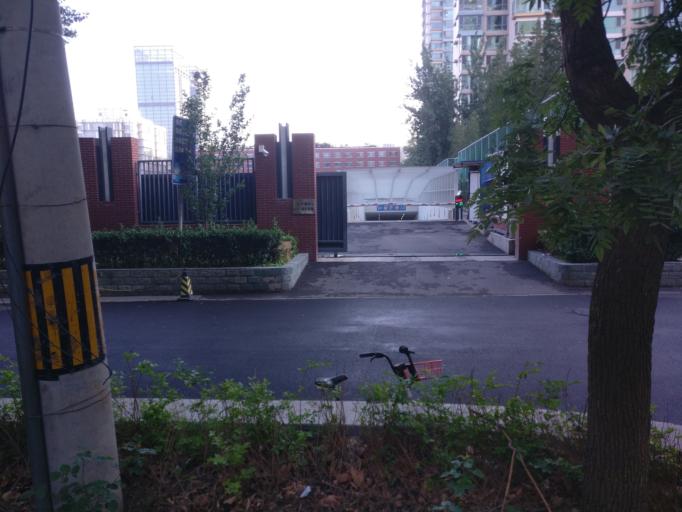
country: CN
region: Beijing
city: Chaowai
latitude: 39.9352
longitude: 116.4345
